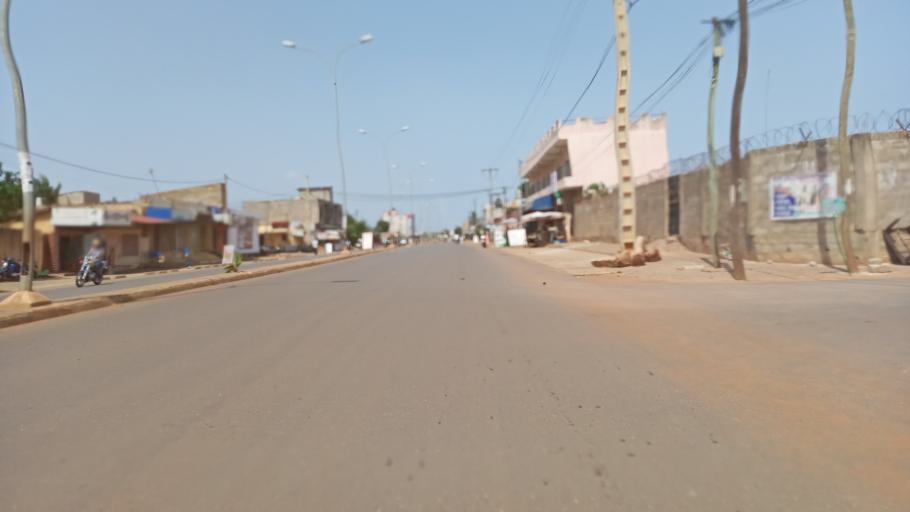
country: TG
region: Maritime
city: Lome
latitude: 6.2253
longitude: 1.1944
